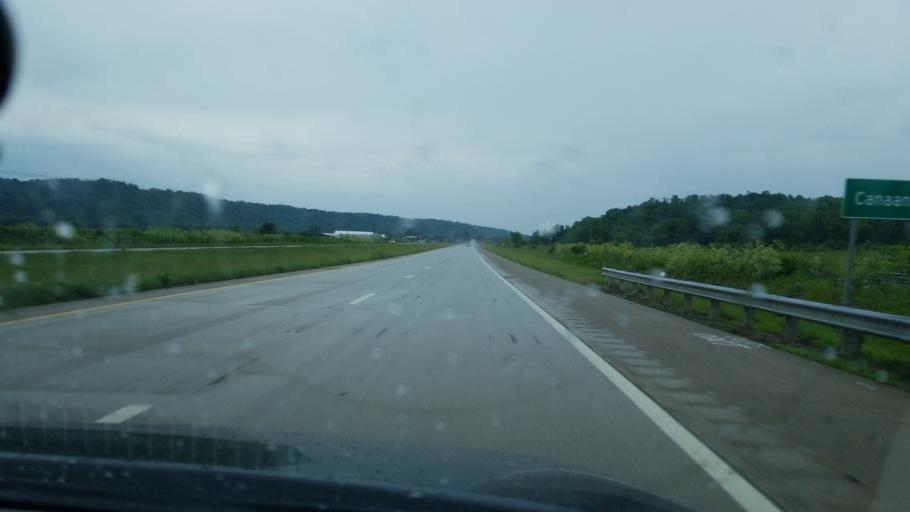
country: US
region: Ohio
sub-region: Athens County
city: Athens
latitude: 39.3085
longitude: -81.9714
